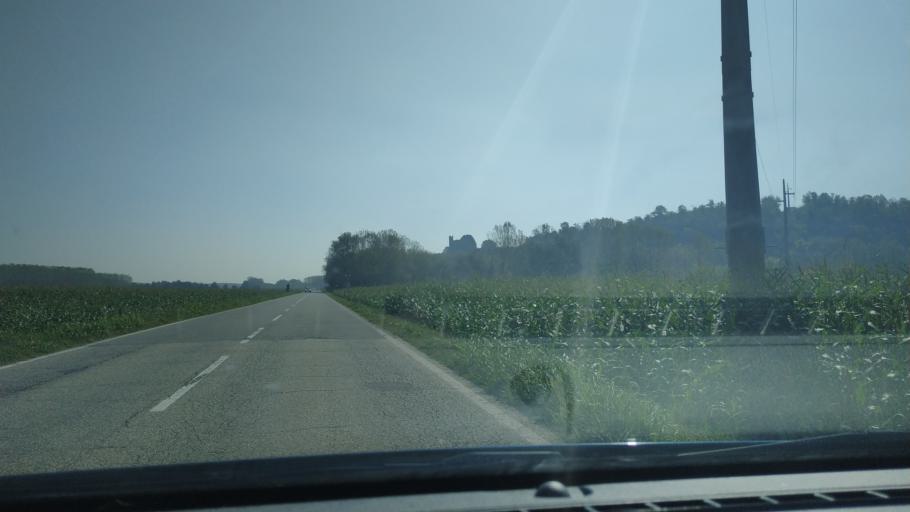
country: IT
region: Piedmont
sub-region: Provincia di Alessandria
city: Pomaro Monferrato
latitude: 45.0689
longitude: 8.5880
